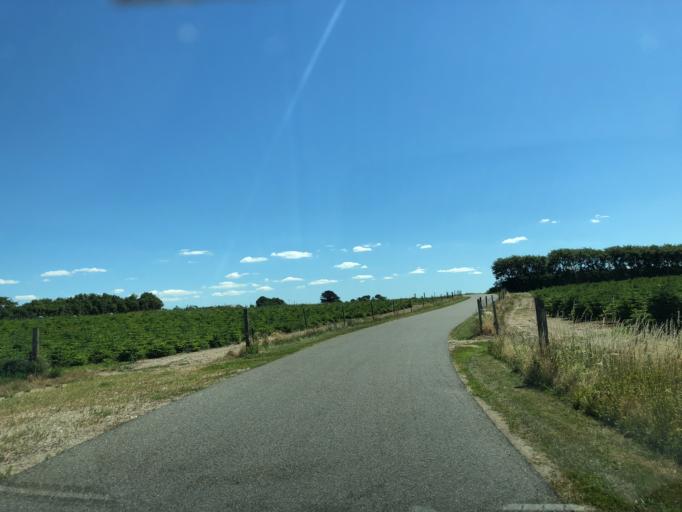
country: DK
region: Central Jutland
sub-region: Viborg Kommune
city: Viborg
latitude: 56.5088
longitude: 9.5175
